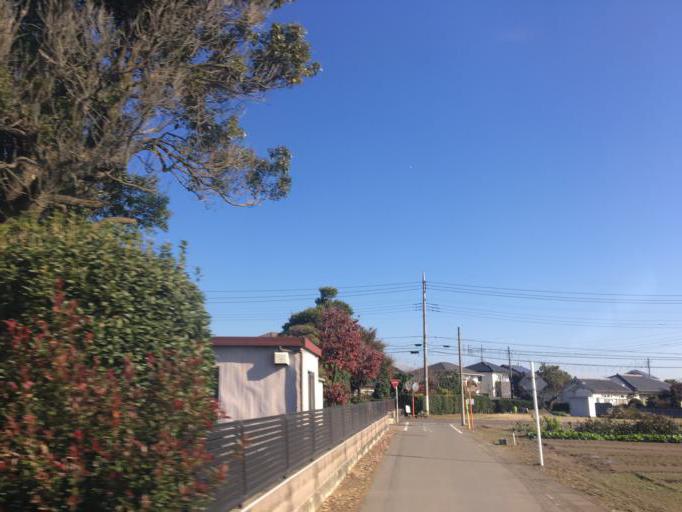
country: JP
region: Gunma
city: Isesaki
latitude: 36.3403
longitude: 139.1678
